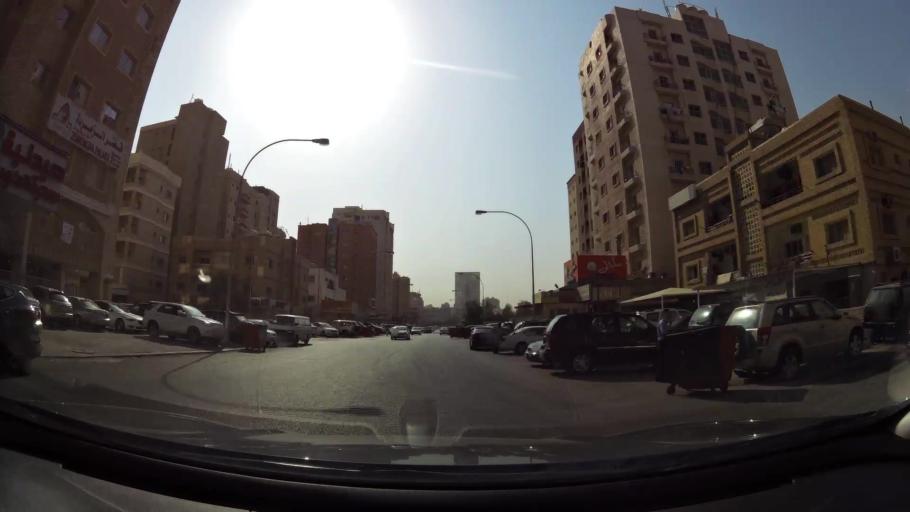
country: KW
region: Muhafazat Hawalli
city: Hawalli
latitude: 29.3286
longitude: 48.0119
